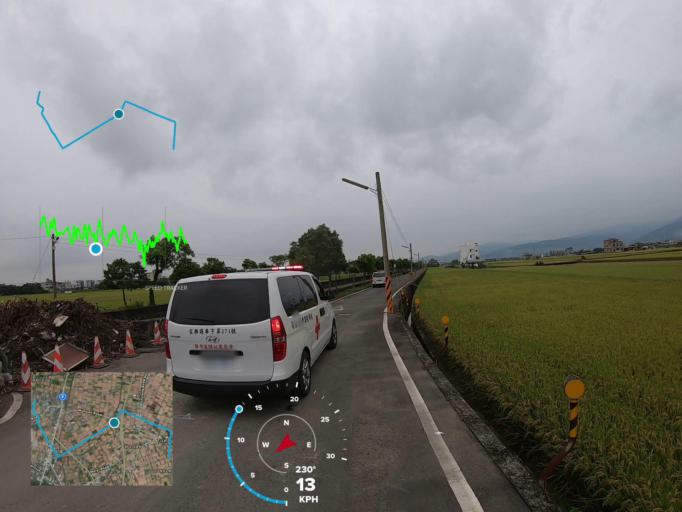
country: TW
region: Taiwan
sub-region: Yilan
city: Yilan
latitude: 24.7811
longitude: 121.7746
